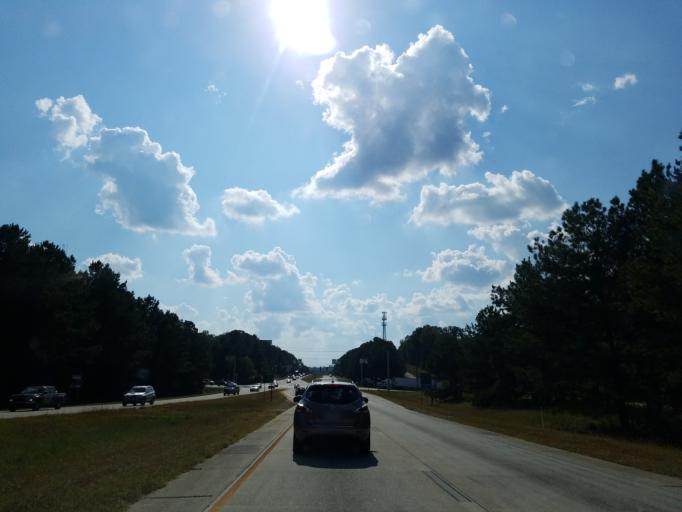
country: US
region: Georgia
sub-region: Barrow County
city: Russell
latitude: 33.9423
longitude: -83.7159
